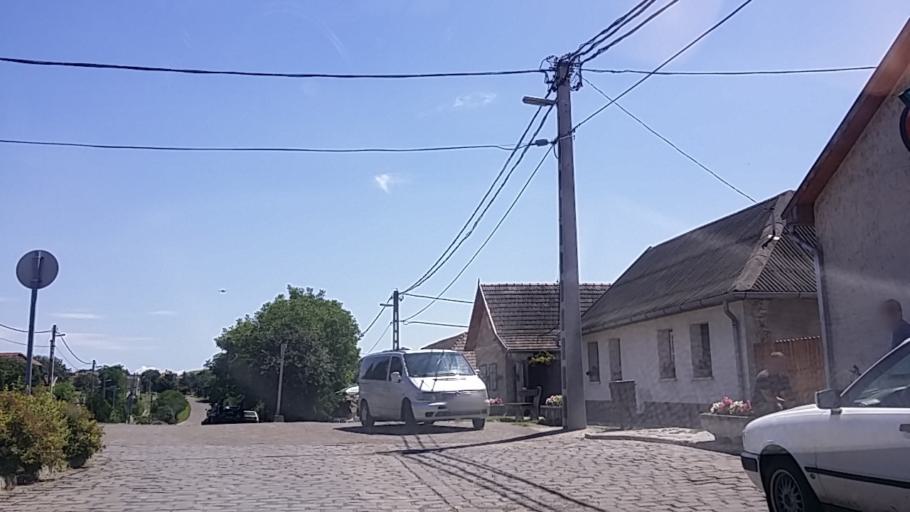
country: HU
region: Pest
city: Szob
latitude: 47.8647
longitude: 18.8704
